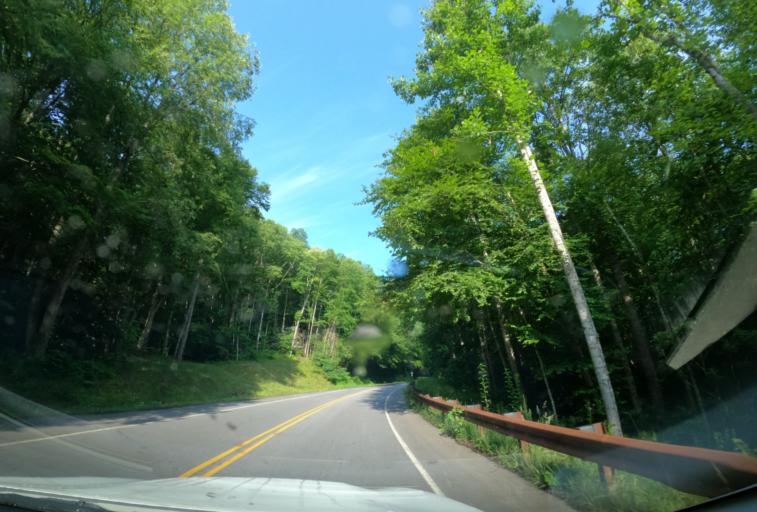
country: US
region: North Carolina
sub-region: Transylvania County
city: Brevard
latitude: 35.2572
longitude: -82.9053
